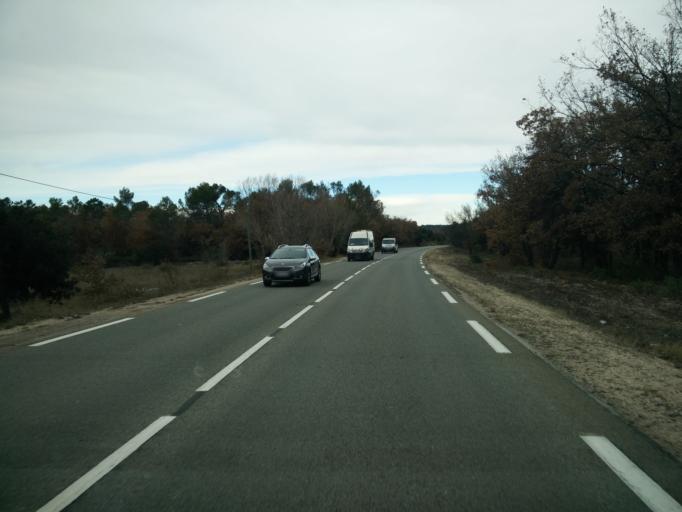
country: FR
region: Provence-Alpes-Cote d'Azur
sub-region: Departement du Var
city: Camps-la-Source
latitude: 43.3705
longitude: 6.0900
